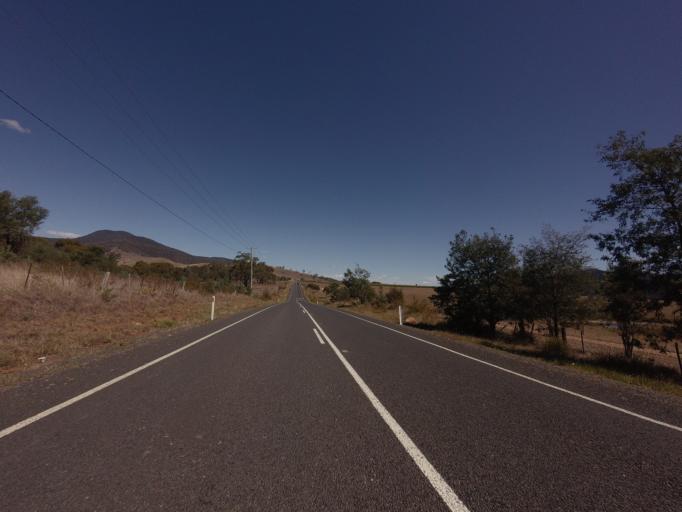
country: AU
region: Tasmania
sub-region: Break O'Day
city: St Helens
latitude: -41.7142
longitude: 147.8371
